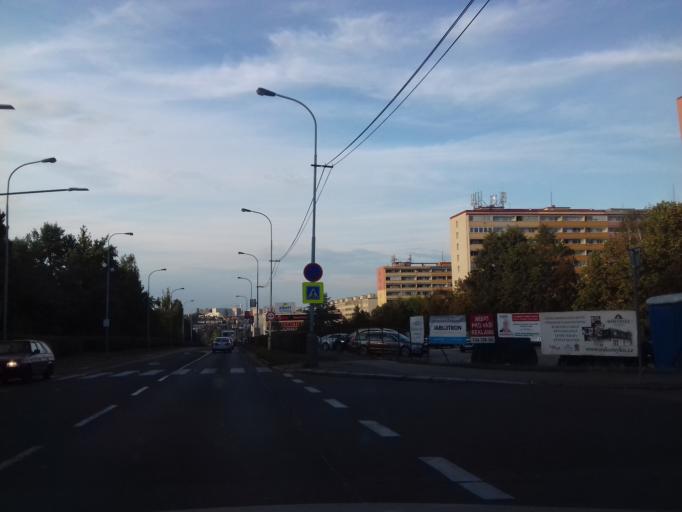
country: CZ
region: Praha
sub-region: Praha 4
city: Hodkovicky
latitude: 50.0244
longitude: 14.4515
